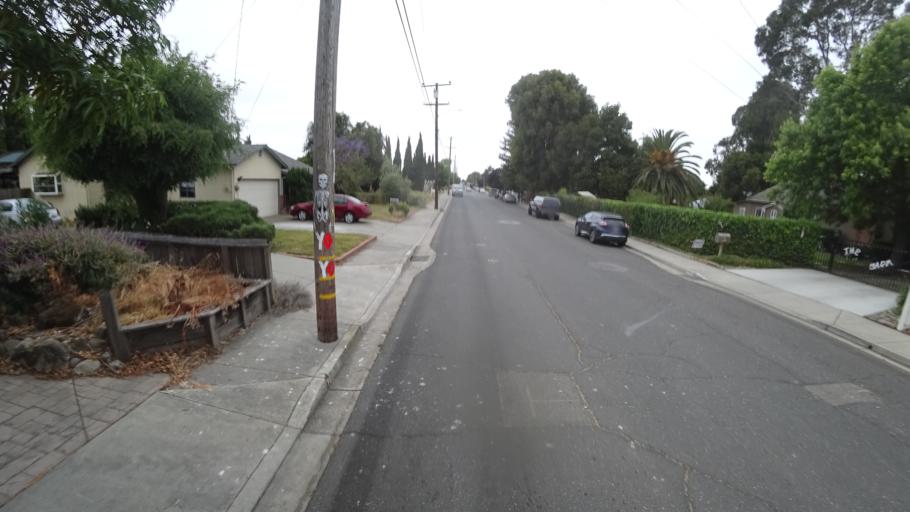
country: US
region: California
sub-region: Alameda County
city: Hayward
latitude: 37.6238
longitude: -122.0681
